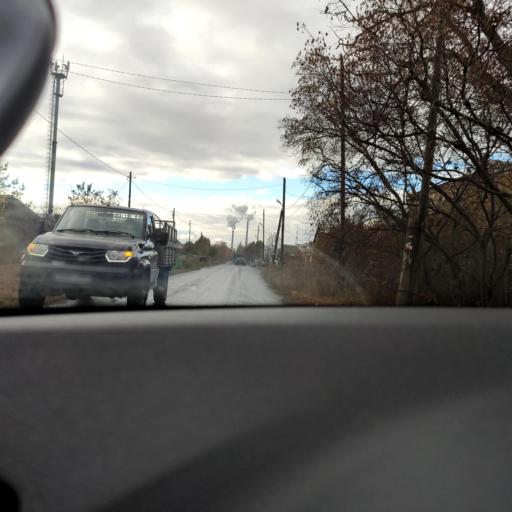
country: RU
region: Samara
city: Petra-Dubrava
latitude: 53.2484
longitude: 50.3264
